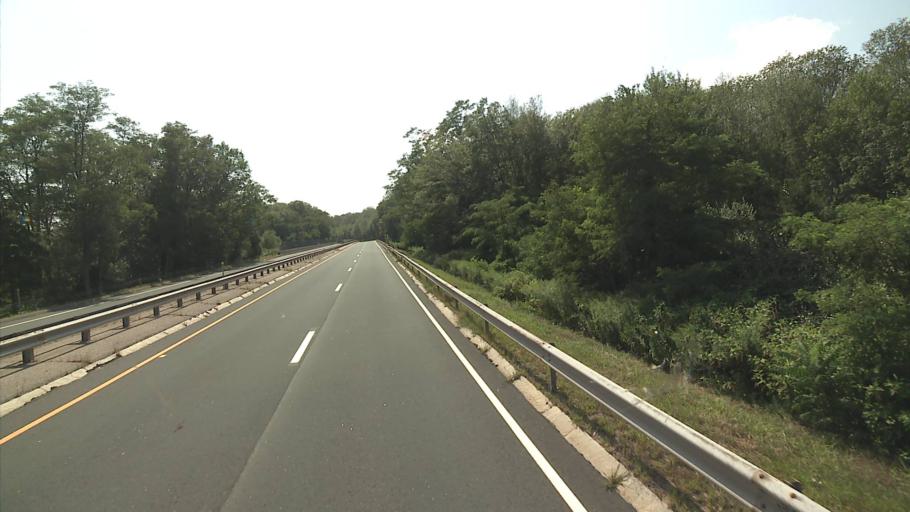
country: US
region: Connecticut
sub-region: Middlesex County
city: Chester Center
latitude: 41.4199
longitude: -72.4924
